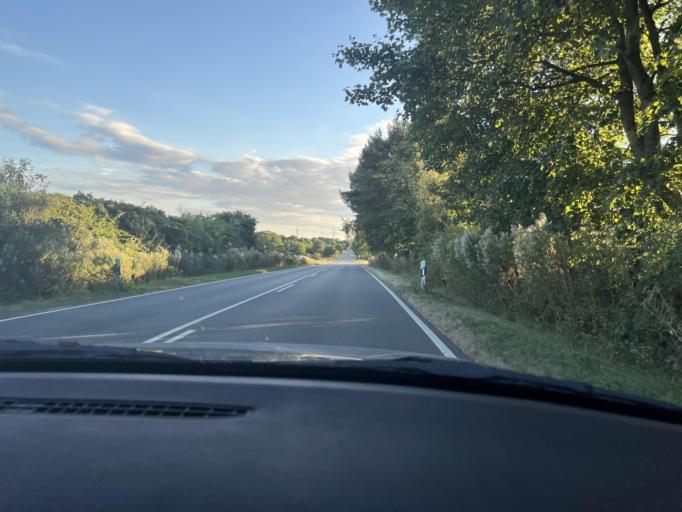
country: DE
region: Schleswig-Holstein
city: Linden
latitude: 54.2478
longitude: 9.1689
